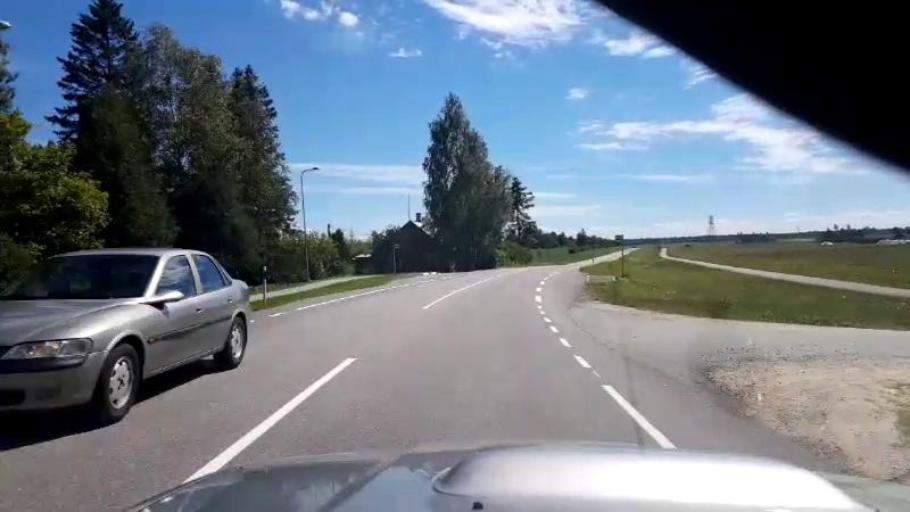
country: EE
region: Jaervamaa
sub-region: Jaerva-Jaani vald
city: Jarva-Jaani
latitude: 59.0291
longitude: 25.8956
